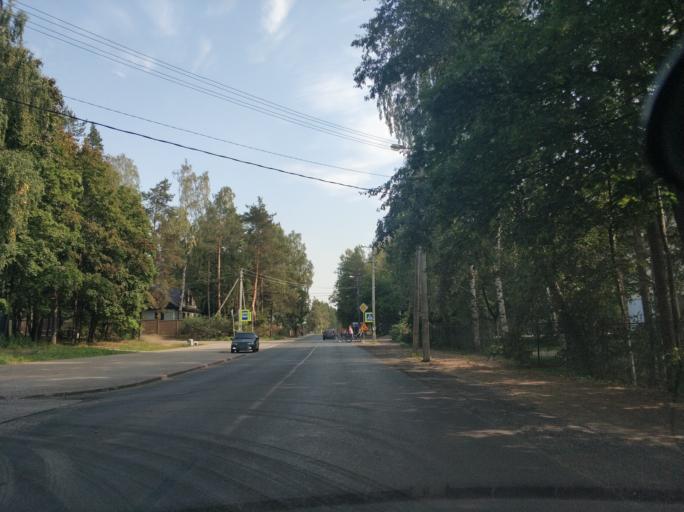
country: RU
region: Leningrad
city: Vsevolozhsk
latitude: 60.0197
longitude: 30.6544
